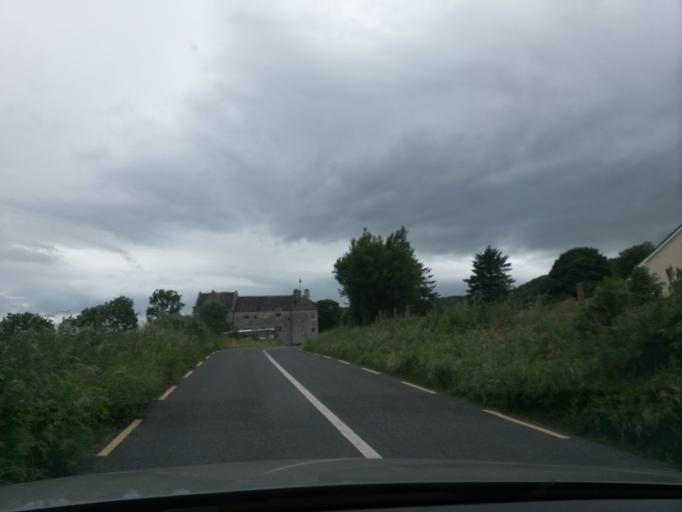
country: IE
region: Connaught
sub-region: Sligo
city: Sligo
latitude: 54.2647
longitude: -8.3325
